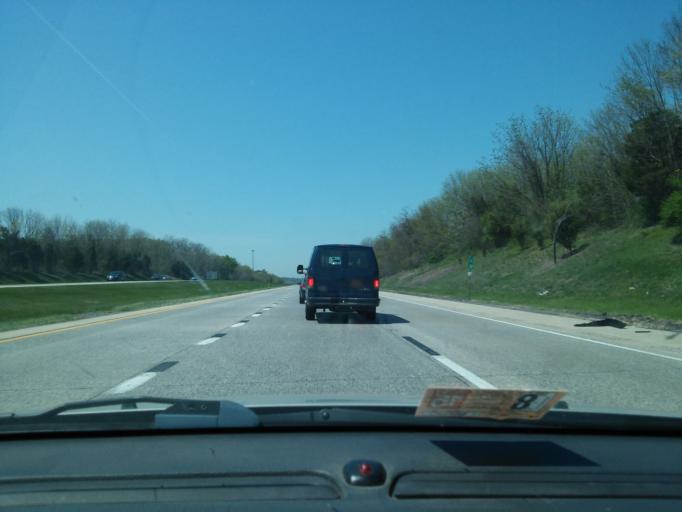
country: US
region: Pennsylvania
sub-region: Lebanon County
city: Jonestown
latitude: 40.4232
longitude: -76.5327
